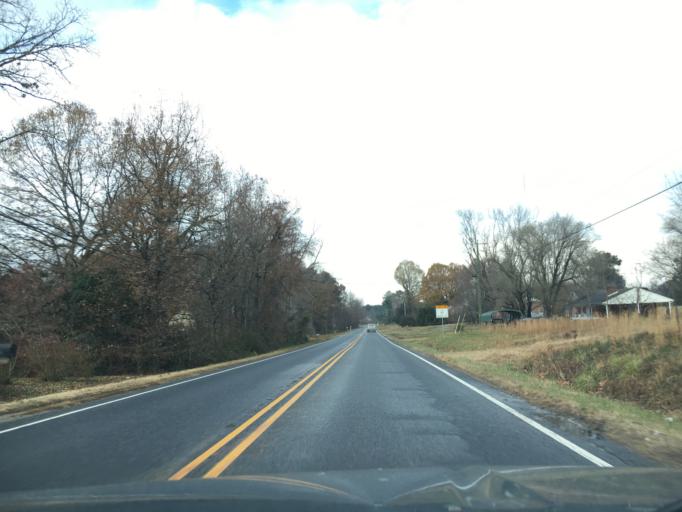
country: US
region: Virginia
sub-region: Prince Edward County
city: Farmville
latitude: 37.3208
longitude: -78.3860
